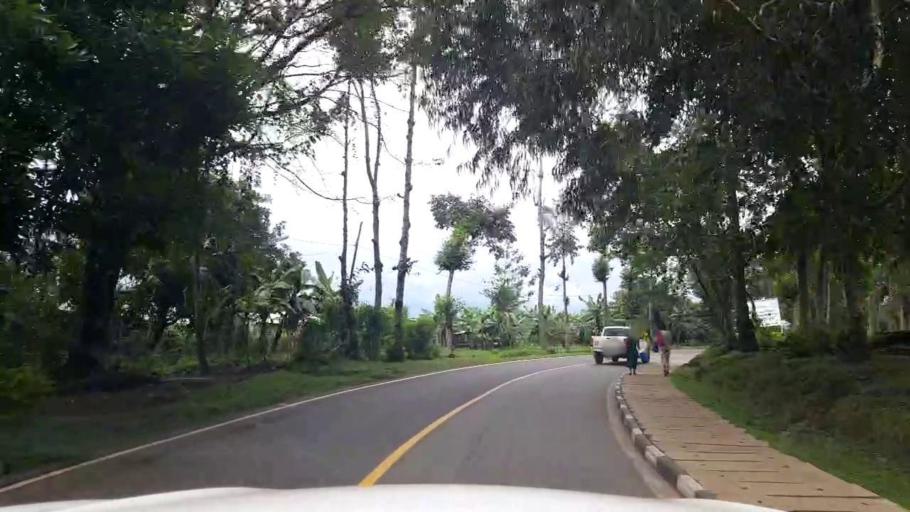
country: RW
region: Northern Province
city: Musanze
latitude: -1.4536
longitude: 29.6019
